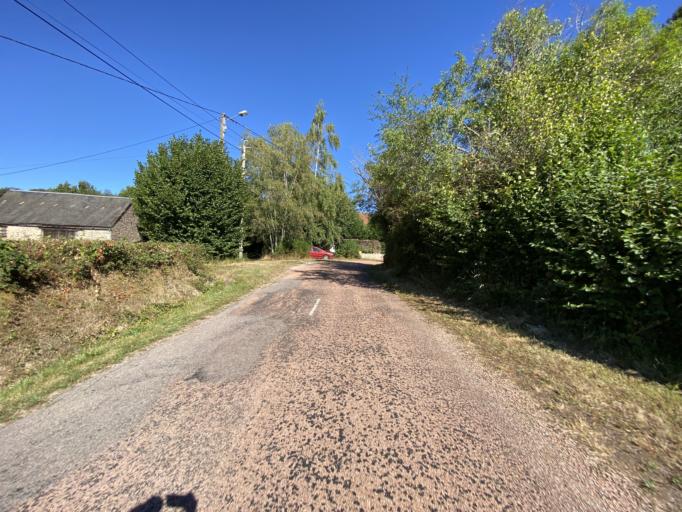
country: FR
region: Bourgogne
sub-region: Departement de la Cote-d'Or
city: Saulieu
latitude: 47.2692
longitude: 4.1742
